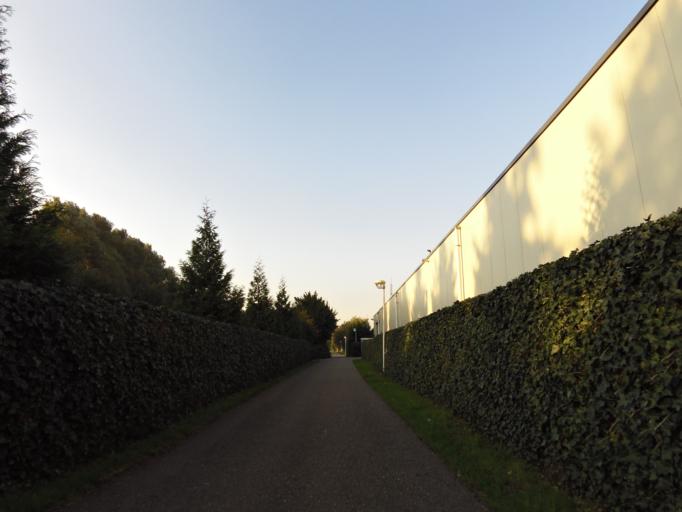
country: NL
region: South Holland
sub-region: Gemeente Kaag en Braassem
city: Oude Wetering
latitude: 52.1717
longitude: 4.6359
